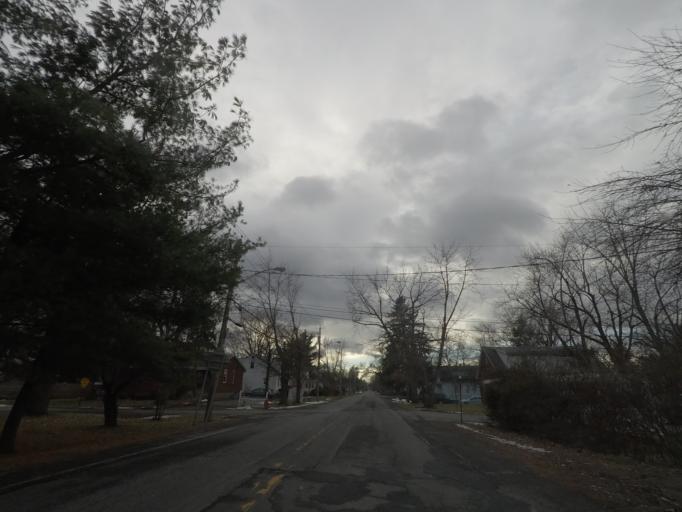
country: US
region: New York
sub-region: Rensselaer County
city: Hampton Manor
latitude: 42.6262
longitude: -73.7270
